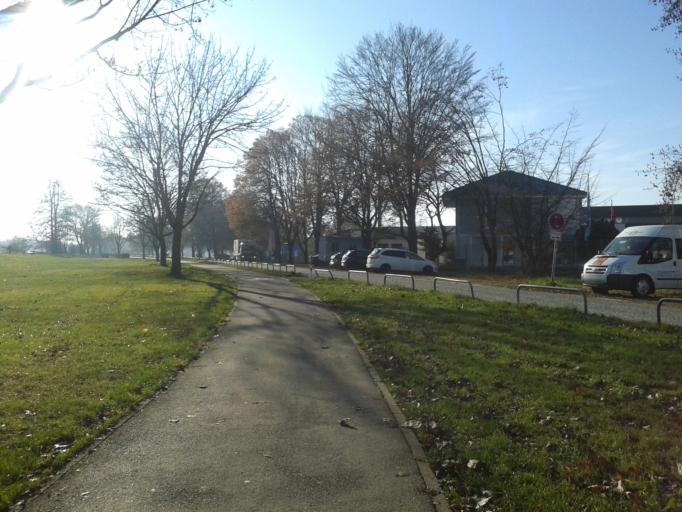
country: DE
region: Bavaria
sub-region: Swabia
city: Neu-Ulm
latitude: 48.4155
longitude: 10.0156
